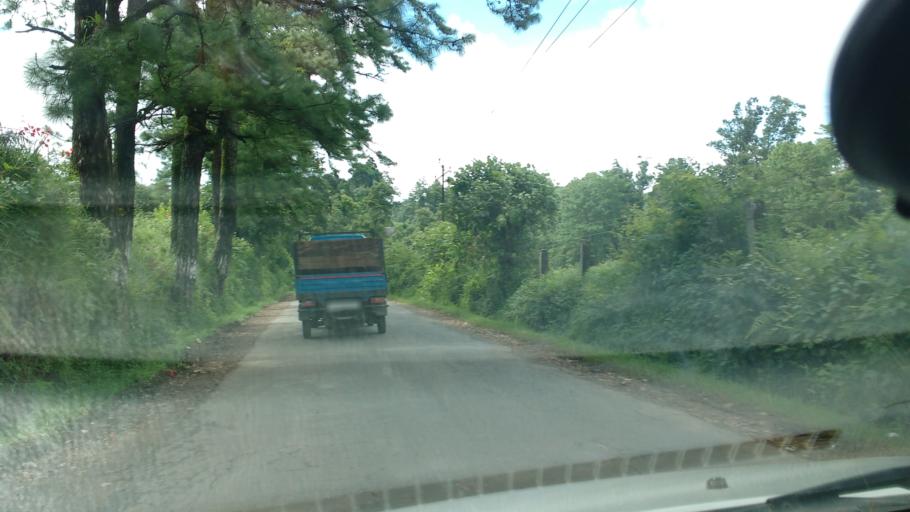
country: IN
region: Meghalaya
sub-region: East Khasi Hills
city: Shillong
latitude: 25.5429
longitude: 91.8476
